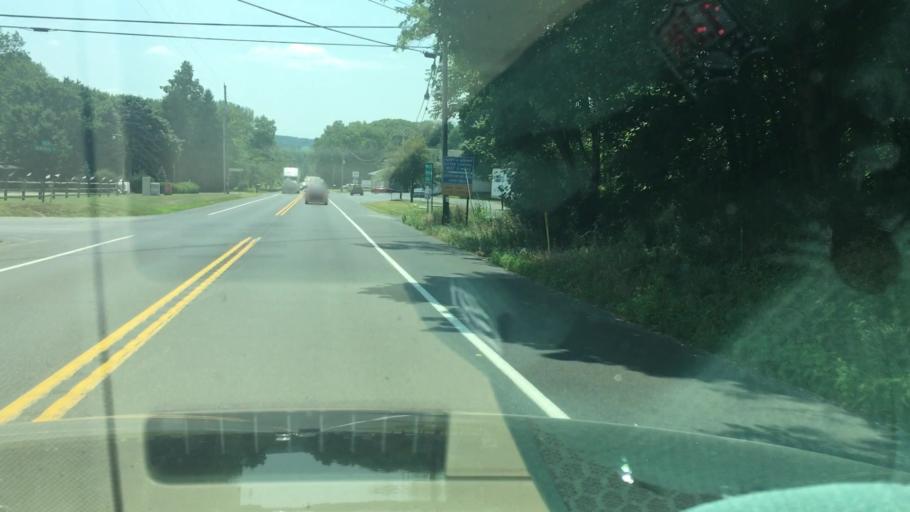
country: US
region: Pennsylvania
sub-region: Lehigh County
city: Schnecksville
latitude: 40.6908
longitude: -75.7482
